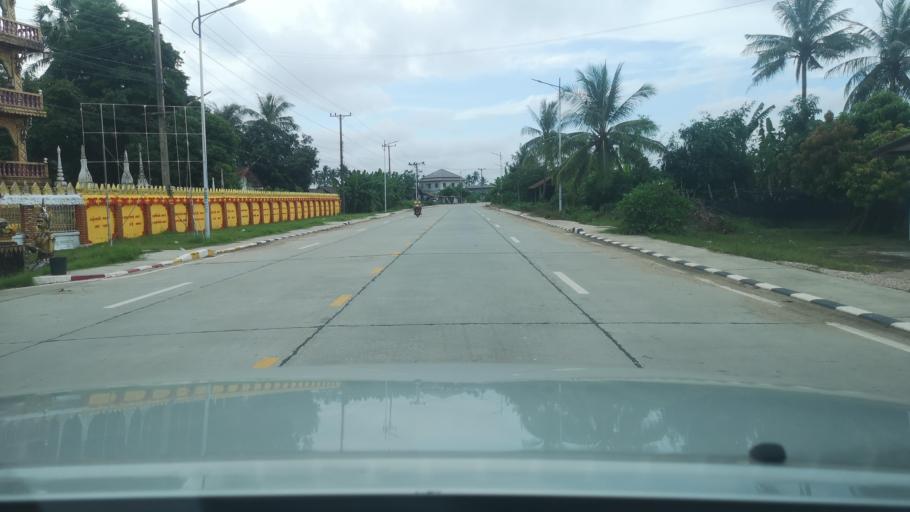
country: TH
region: Nong Khai
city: Tha Bo
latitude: 17.8224
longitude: 102.6623
